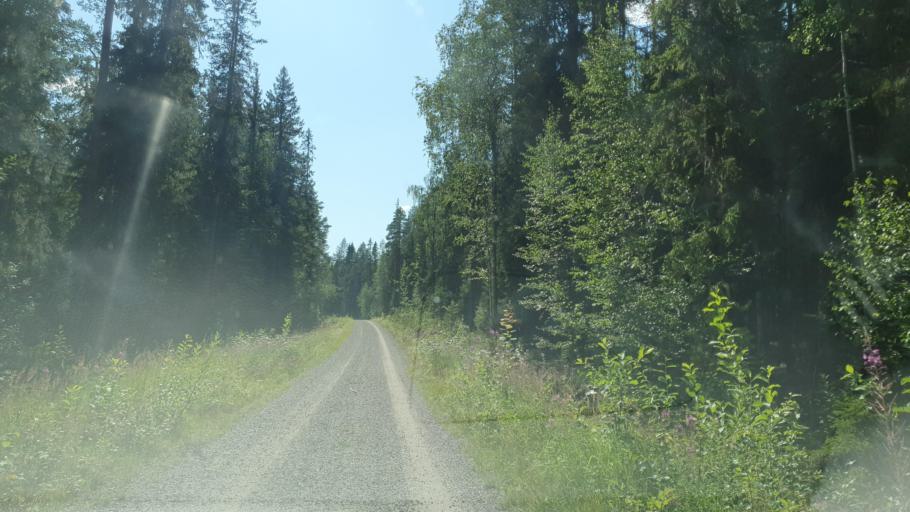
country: FI
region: Kainuu
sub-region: Kehys-Kainuu
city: Kuhmo
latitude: 63.9758
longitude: 29.5402
